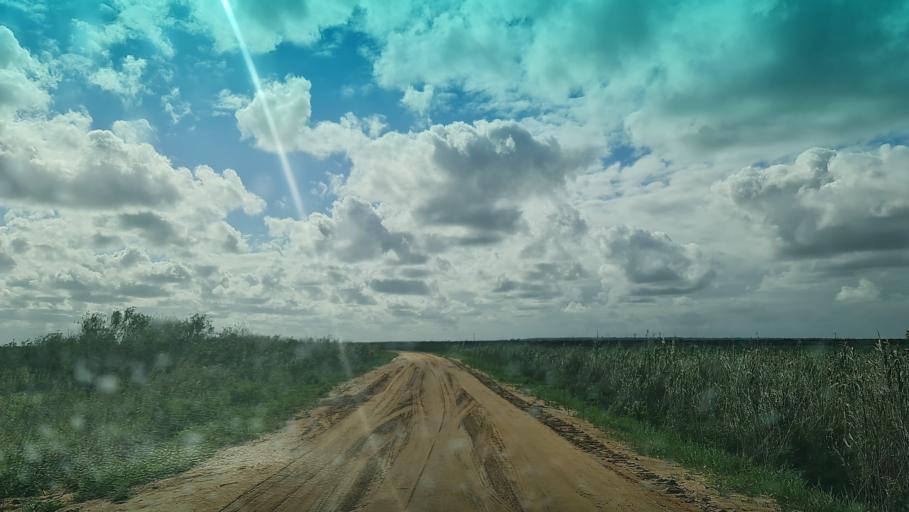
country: MZ
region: Maputo
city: Manhica
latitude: -25.4337
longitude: 32.8655
